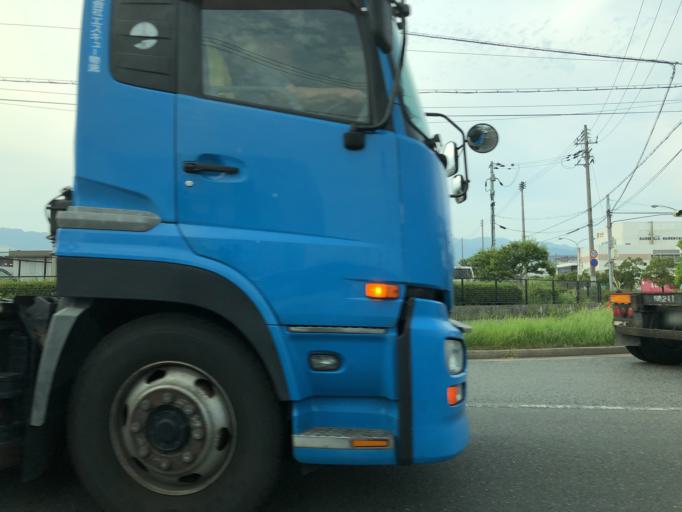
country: JP
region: Hyogo
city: Ashiya
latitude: 34.6883
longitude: 135.2607
